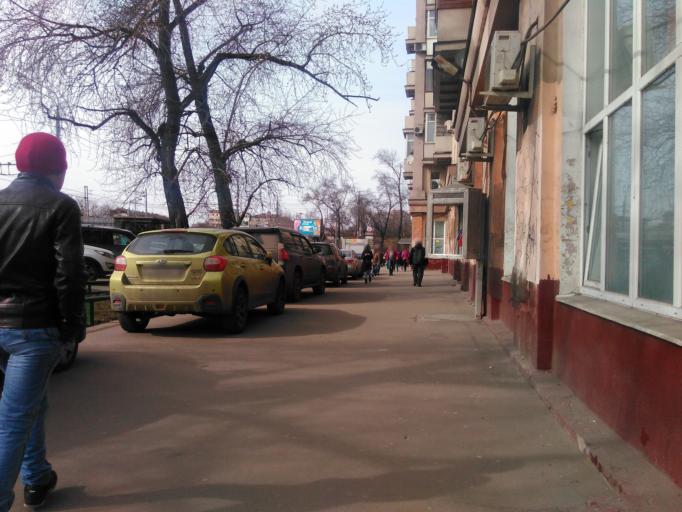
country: RU
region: Moscow
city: Mar'ina Roshcha
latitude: 55.8073
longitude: 37.5820
